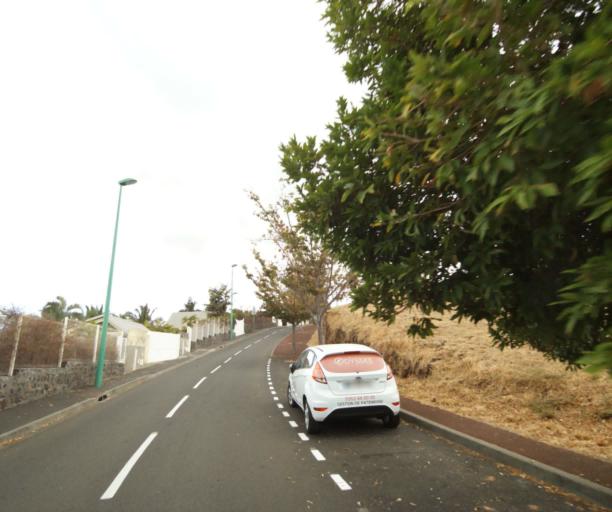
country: RE
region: Reunion
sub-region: Reunion
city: Saint-Paul
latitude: -21.0608
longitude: 55.2260
